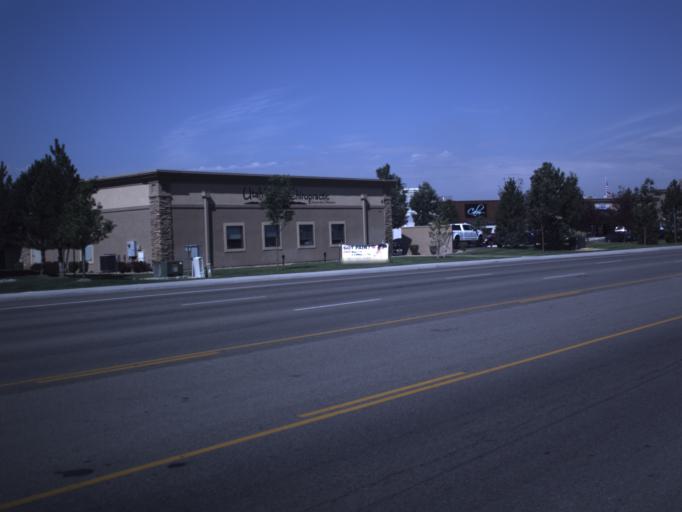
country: US
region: Utah
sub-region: Utah County
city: Pleasant Grove
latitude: 40.3624
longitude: -111.7482
